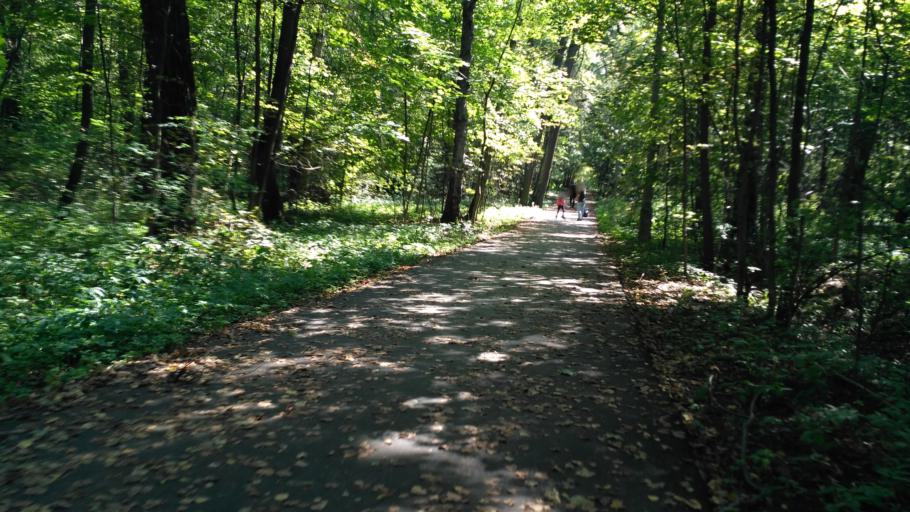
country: RU
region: Moscow
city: Ryazanskiy
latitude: 55.7752
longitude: 37.7592
